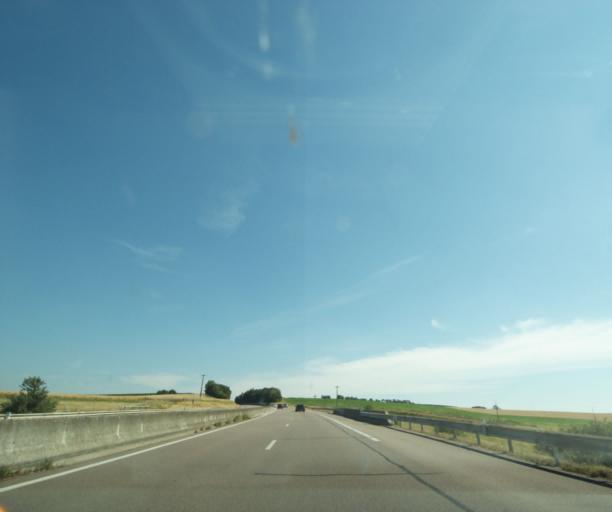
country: FR
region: Lorraine
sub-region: Departement des Vosges
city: Chatenois
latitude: 48.3752
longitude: 5.8797
